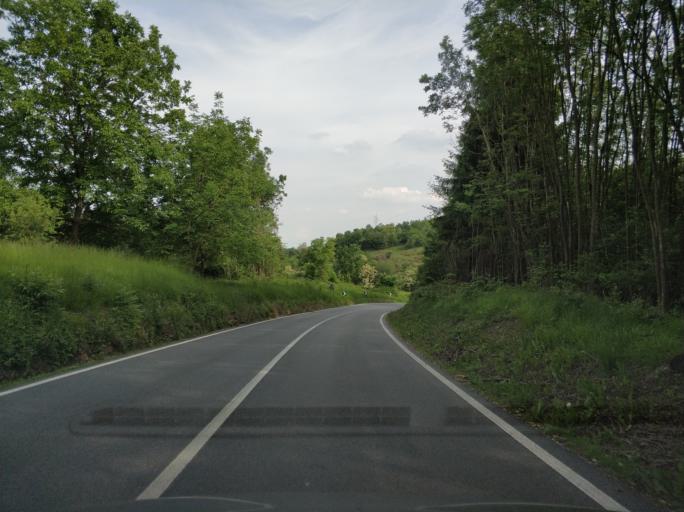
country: IT
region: Piedmont
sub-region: Provincia di Torino
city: Corio
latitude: 45.3019
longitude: 7.5416
